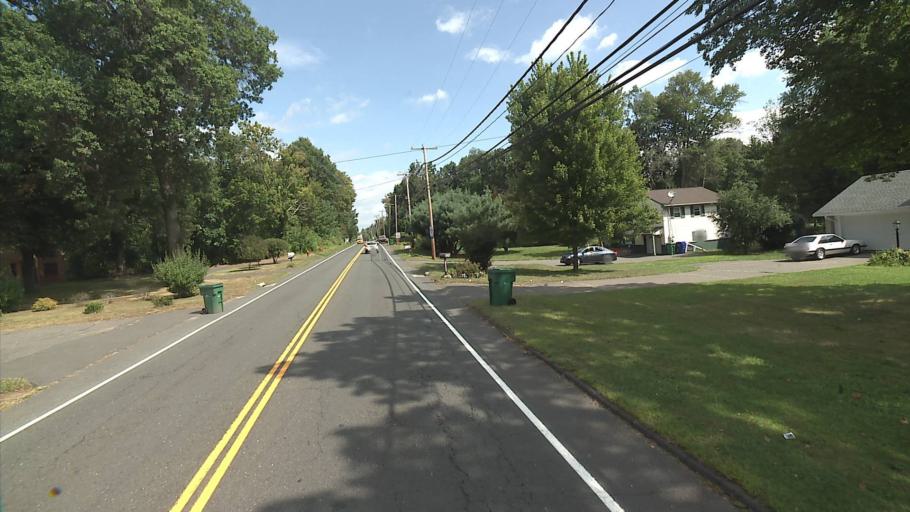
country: US
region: Connecticut
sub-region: Hartford County
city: Blue Hills
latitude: 41.8206
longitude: -72.7386
